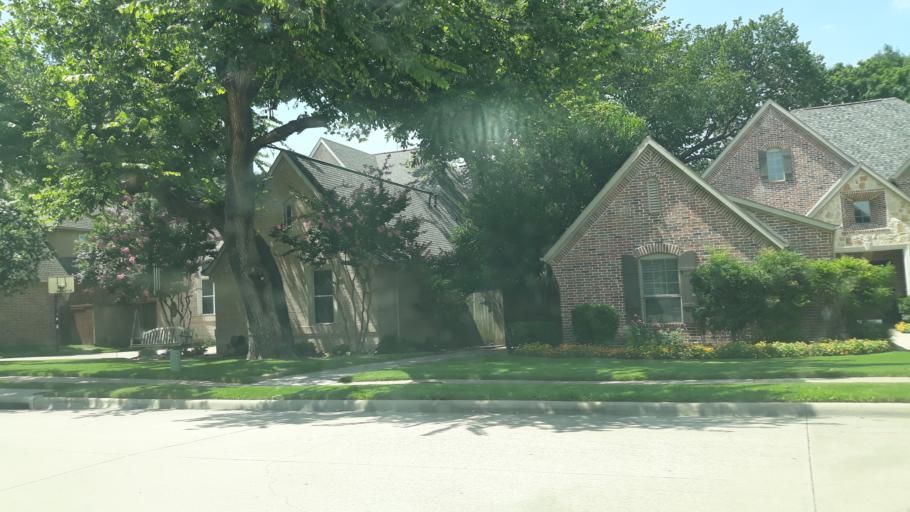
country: US
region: Texas
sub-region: Dallas County
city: Coppell
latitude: 32.9557
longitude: -97.0028
